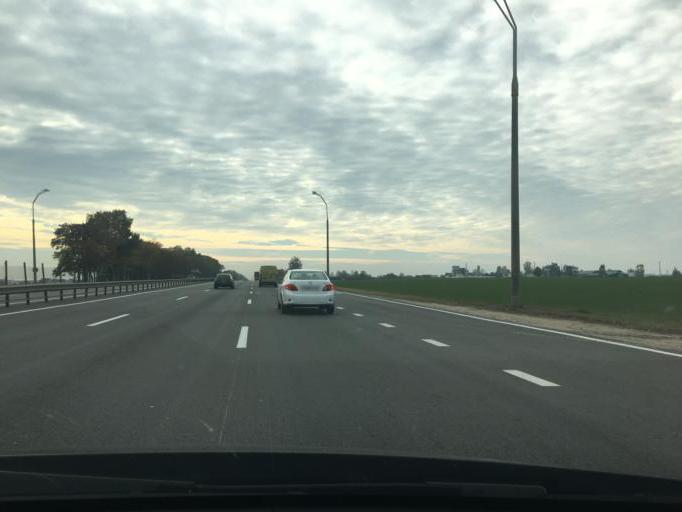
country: BY
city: Fanipol
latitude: 53.7680
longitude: 27.3459
